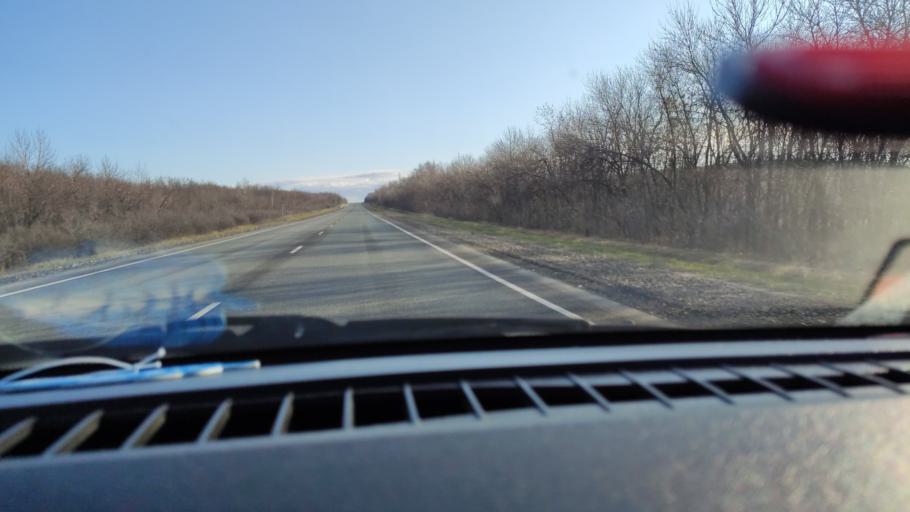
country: RU
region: Saratov
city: Khvalynsk
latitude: 52.6153
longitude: 48.1651
